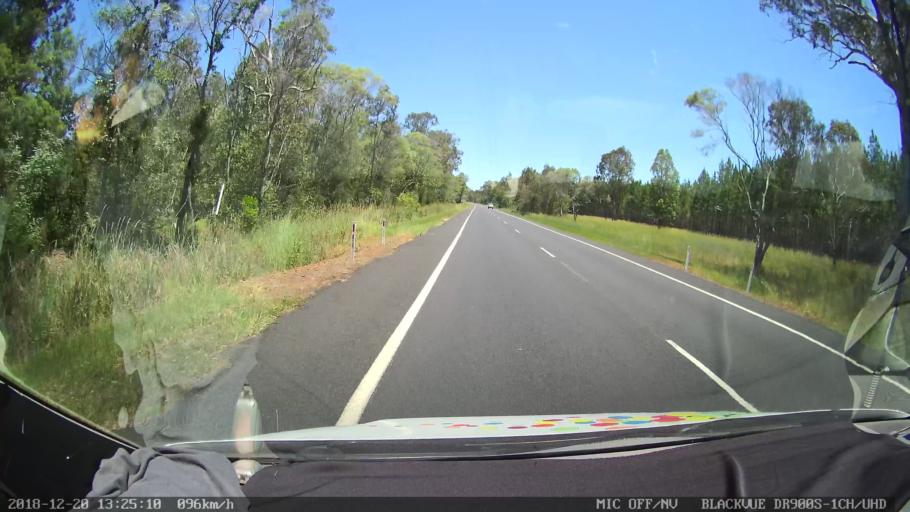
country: AU
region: New South Wales
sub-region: Richmond Valley
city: Casino
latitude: -29.1273
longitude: 152.9974
